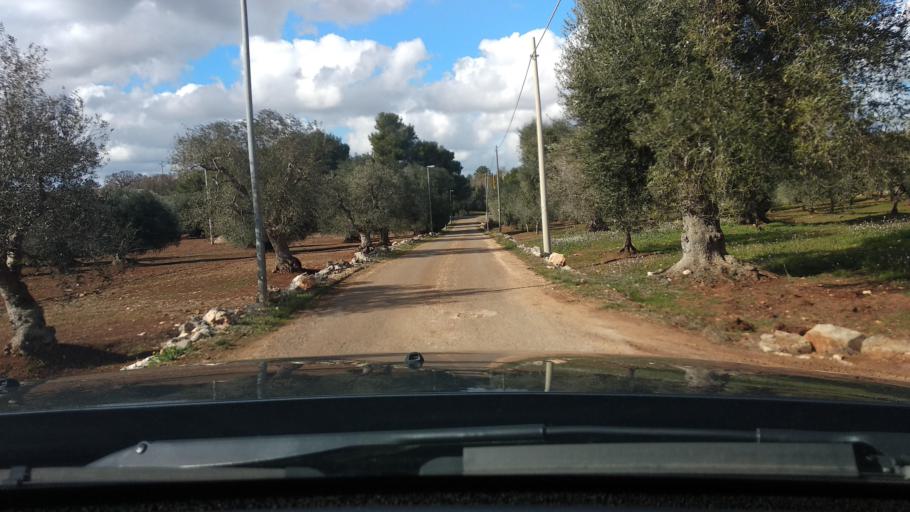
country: IT
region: Apulia
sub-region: Provincia di Brindisi
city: Casalini
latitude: 40.6955
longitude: 17.4840
